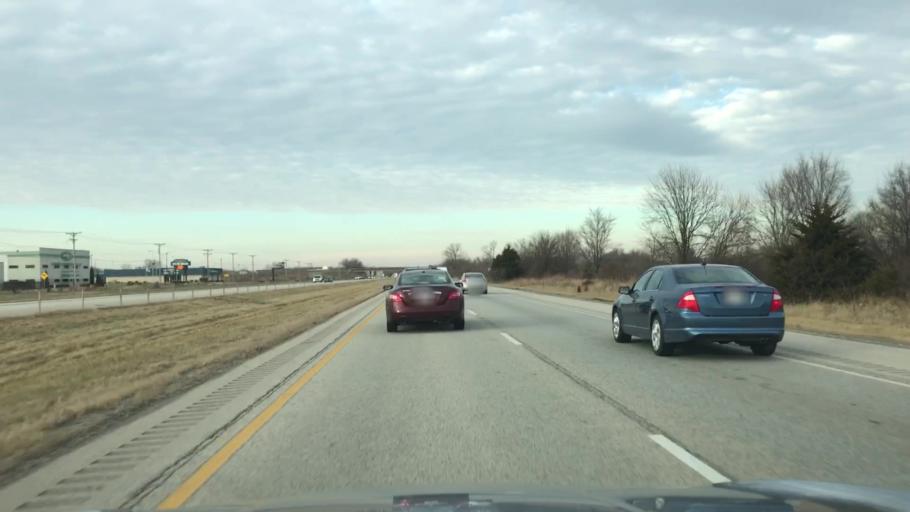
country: US
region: Illinois
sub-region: Sangamon County
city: Grandview
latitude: 39.8406
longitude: -89.5937
